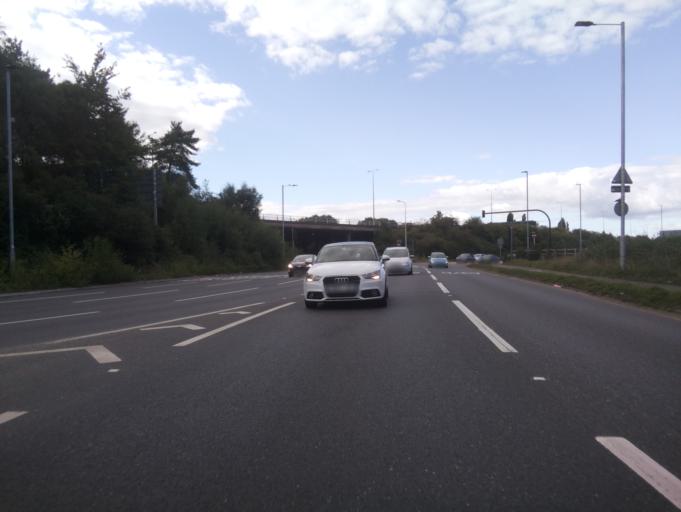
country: GB
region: England
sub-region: Devon
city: Topsham
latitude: 50.7125
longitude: -3.4625
